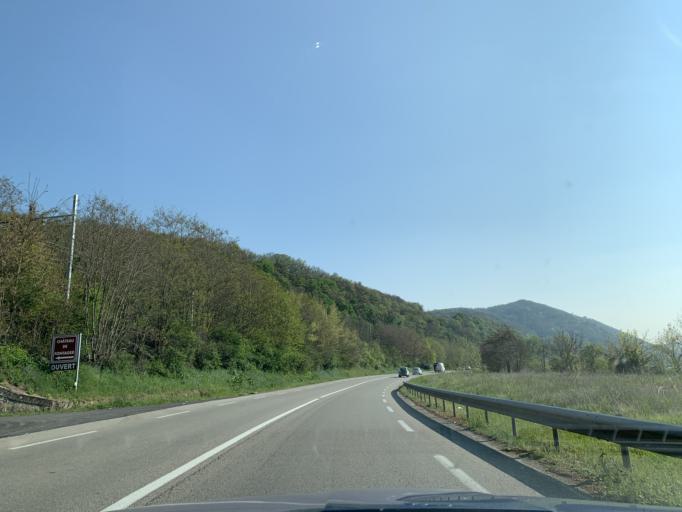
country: FR
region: Rhone-Alpes
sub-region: Departement de la Drome
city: Saint-Vallier
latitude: 45.1566
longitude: 4.8328
